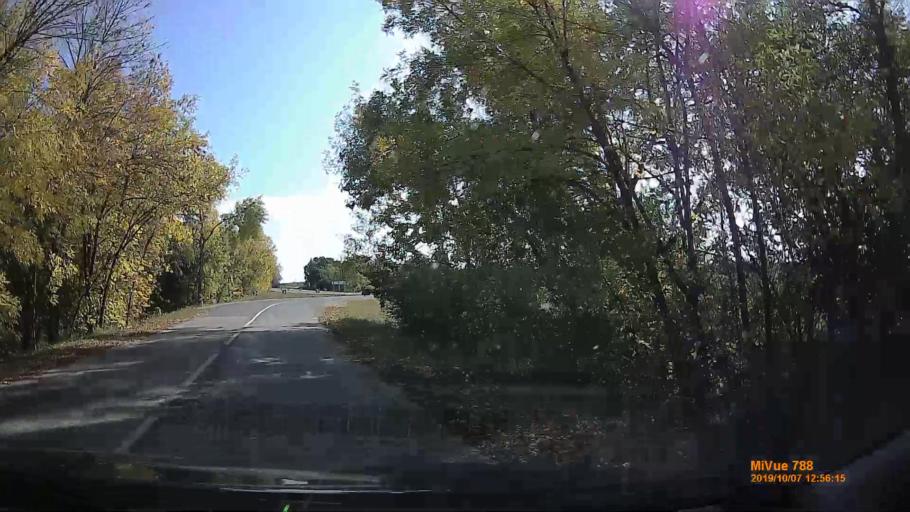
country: HU
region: Jasz-Nagykun-Szolnok
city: Cserkeszolo
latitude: 46.8777
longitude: 20.1459
